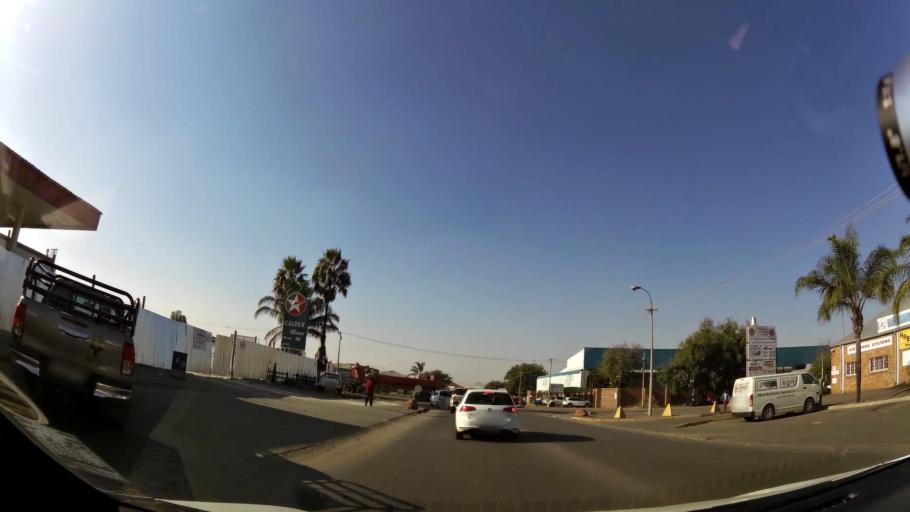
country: ZA
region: North-West
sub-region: Bojanala Platinum District Municipality
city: Rustenburg
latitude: -25.6671
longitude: 27.2595
